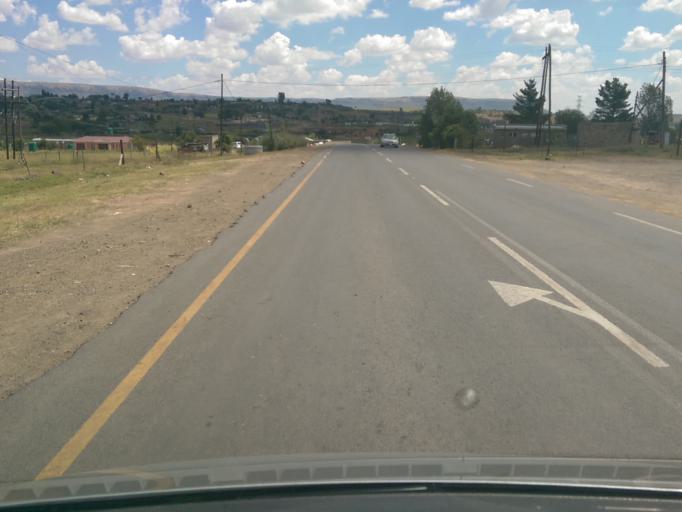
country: LS
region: Maseru
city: Maseru
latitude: -29.4032
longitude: 27.5695
